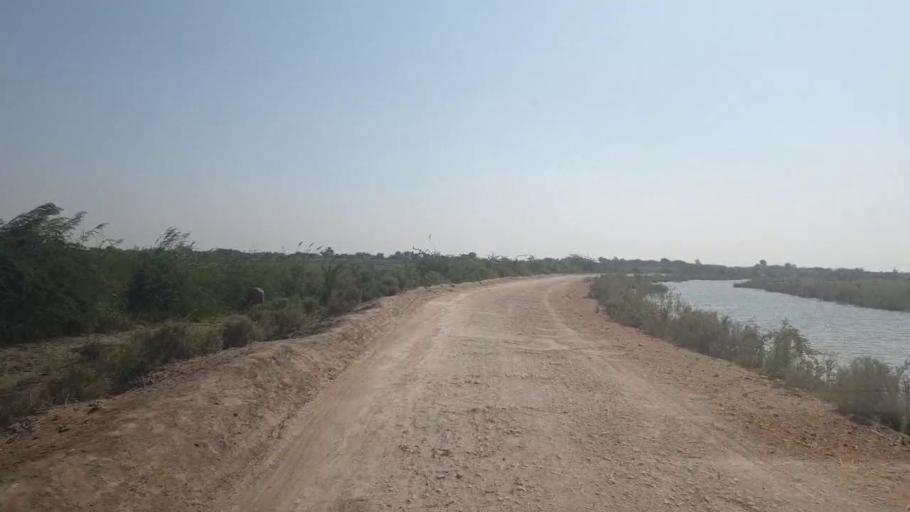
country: PK
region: Sindh
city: Badin
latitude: 24.6509
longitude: 68.9167
